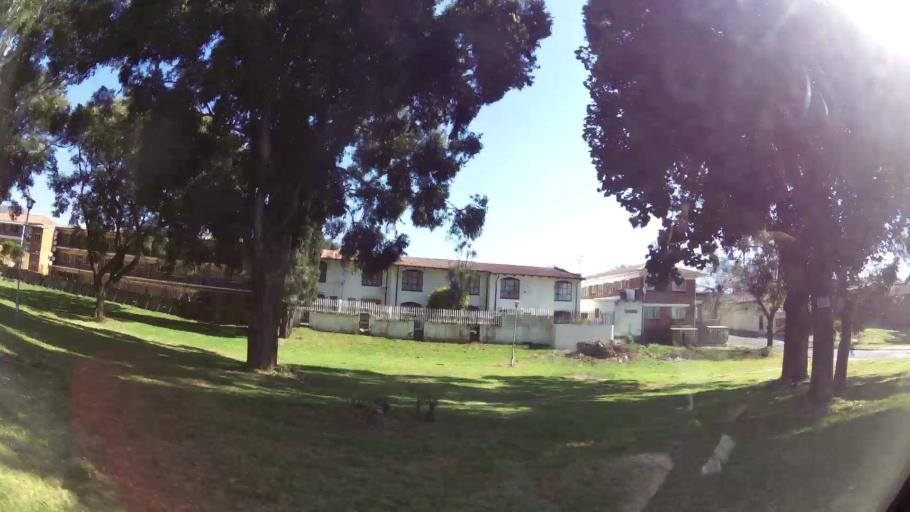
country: ZA
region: Gauteng
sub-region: City of Johannesburg Metropolitan Municipality
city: Johannesburg
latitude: -26.2466
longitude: 28.0585
